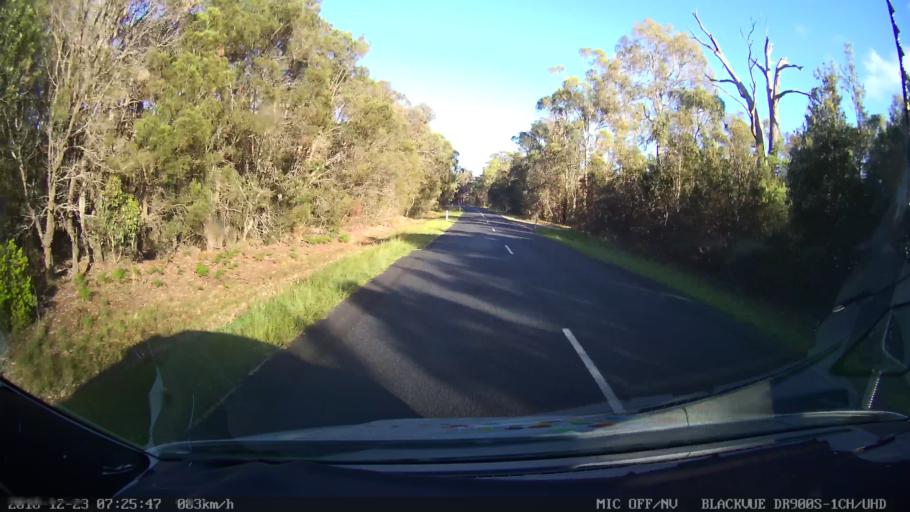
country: AU
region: New South Wales
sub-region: Armidale Dumaresq
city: Enmore
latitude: -30.4958
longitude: 152.2069
